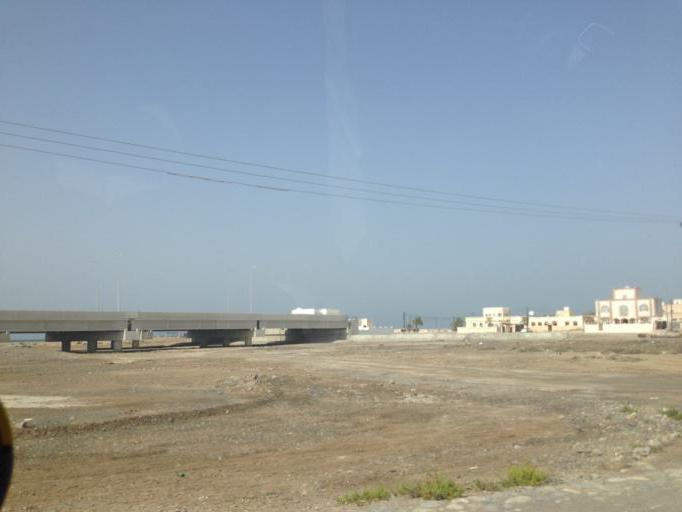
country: OM
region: Al Batinah
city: Barka'
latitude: 23.7061
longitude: 57.9208
